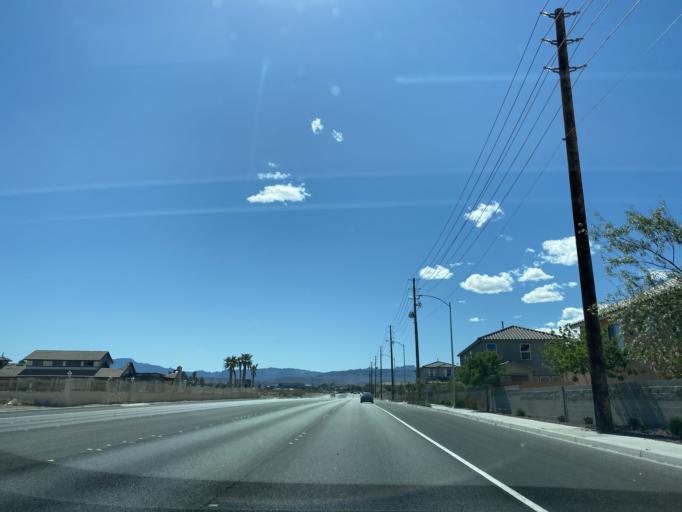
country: US
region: Nevada
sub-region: Clark County
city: Spring Valley
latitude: 36.0858
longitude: -115.2193
